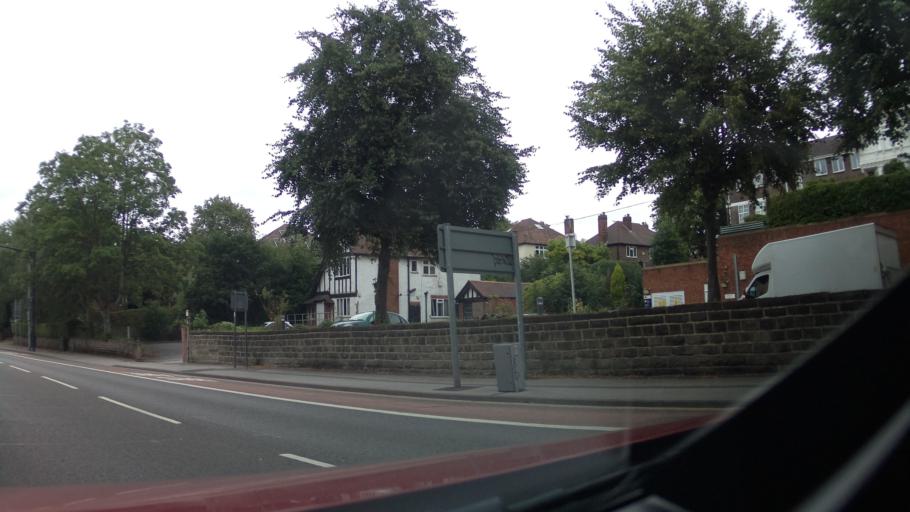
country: GB
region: England
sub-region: Nottinghamshire
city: Arnold
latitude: 52.9904
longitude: -1.1400
